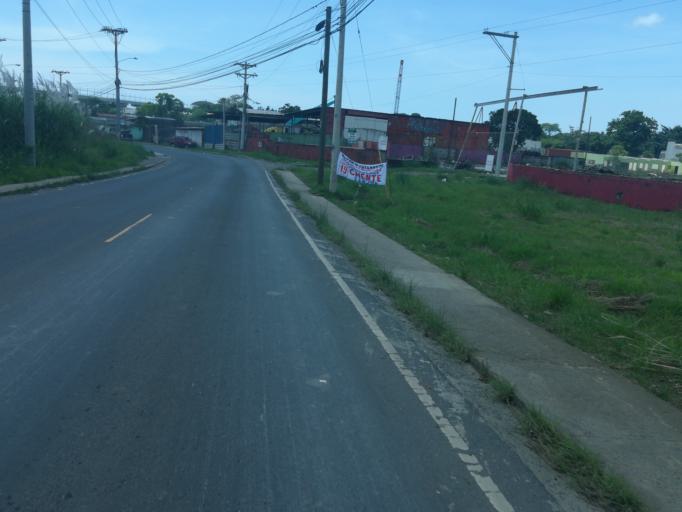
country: PA
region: Panama
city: Tocumen
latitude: 9.0865
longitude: -79.3992
